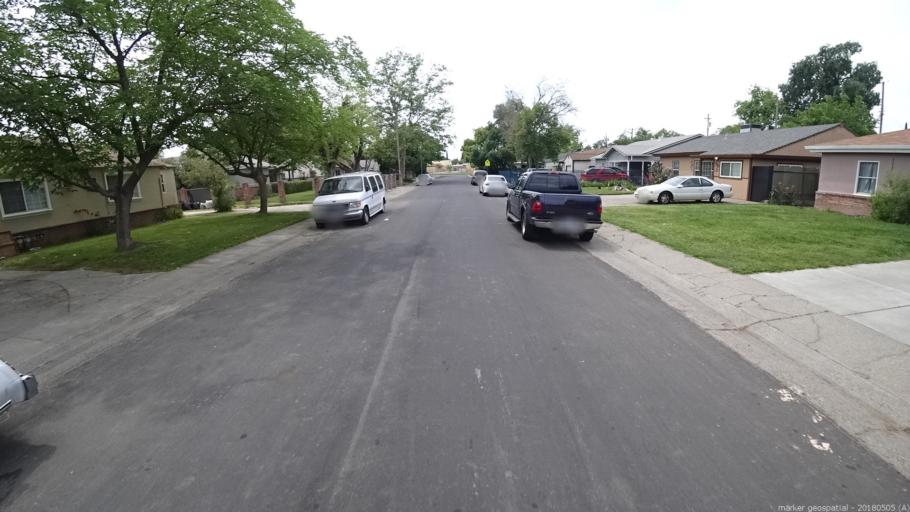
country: US
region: California
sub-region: Sacramento County
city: Arden-Arcade
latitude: 38.6356
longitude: -121.4244
